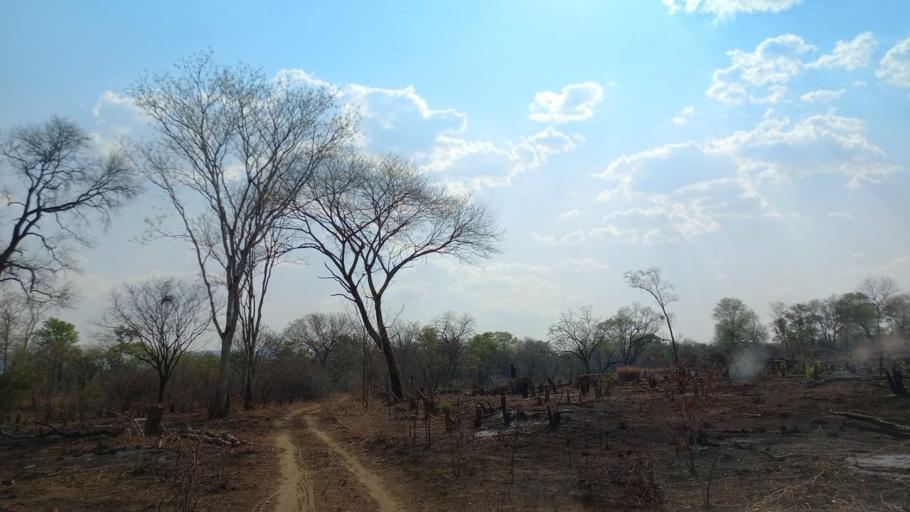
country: ZM
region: Lusaka
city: Luangwa
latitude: -15.1043
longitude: 30.1274
